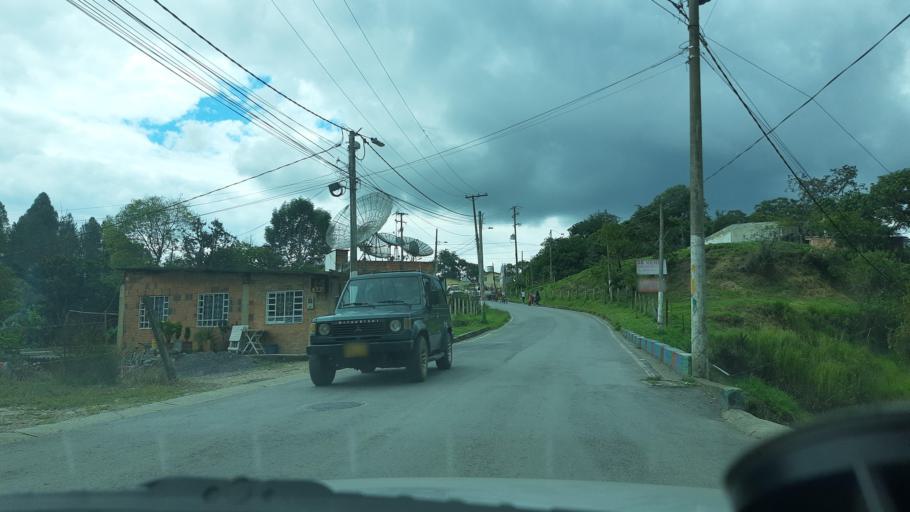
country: CO
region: Boyaca
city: Moniquira
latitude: 5.8808
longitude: -73.5723
